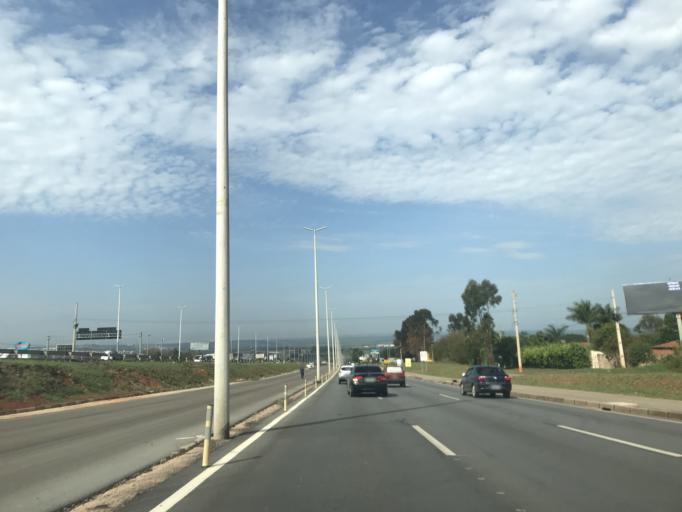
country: BR
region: Federal District
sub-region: Brasilia
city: Brasilia
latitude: -15.6940
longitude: -47.8719
